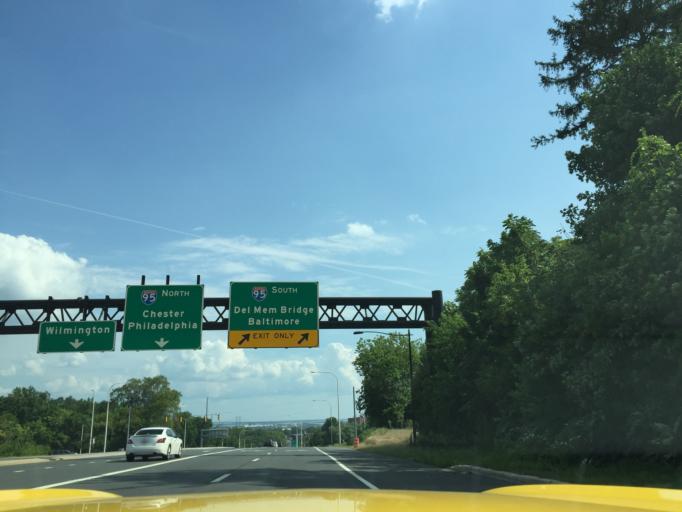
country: US
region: Delaware
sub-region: New Castle County
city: Wilmington
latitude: 39.7699
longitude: -75.5437
